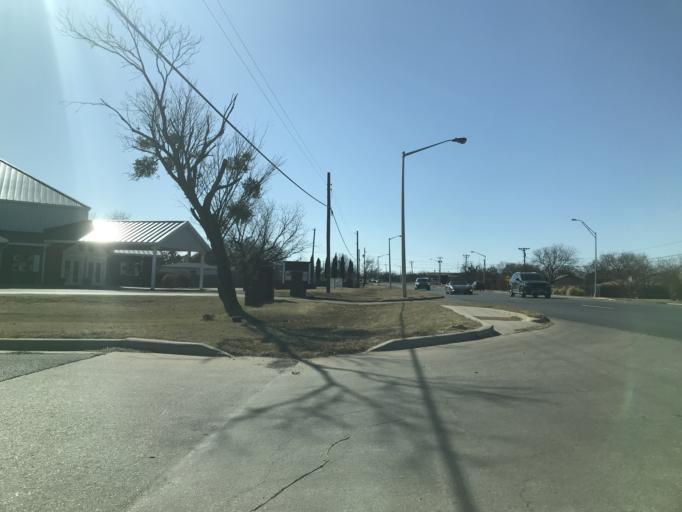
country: US
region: Texas
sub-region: Taylor County
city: Abilene
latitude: 32.3820
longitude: -99.7698
